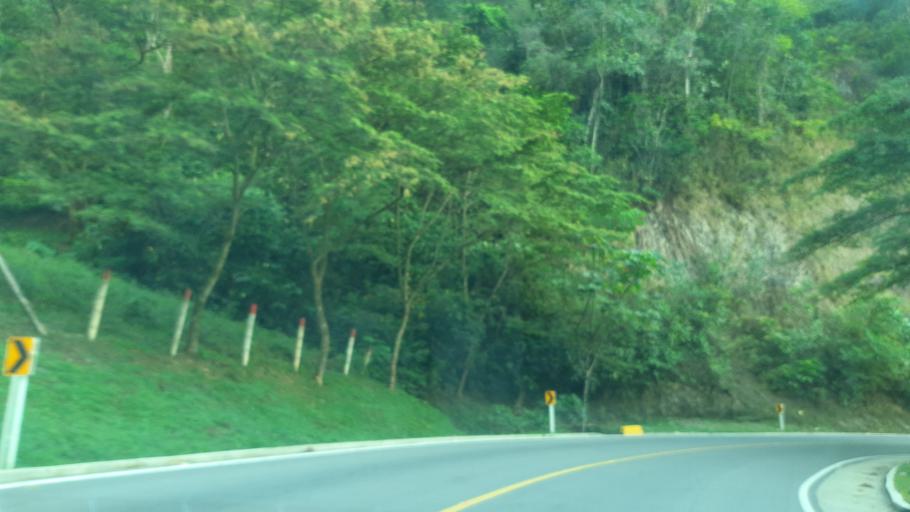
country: CO
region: Boyaca
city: San Luis de Gaceno
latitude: 4.8347
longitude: -73.2070
